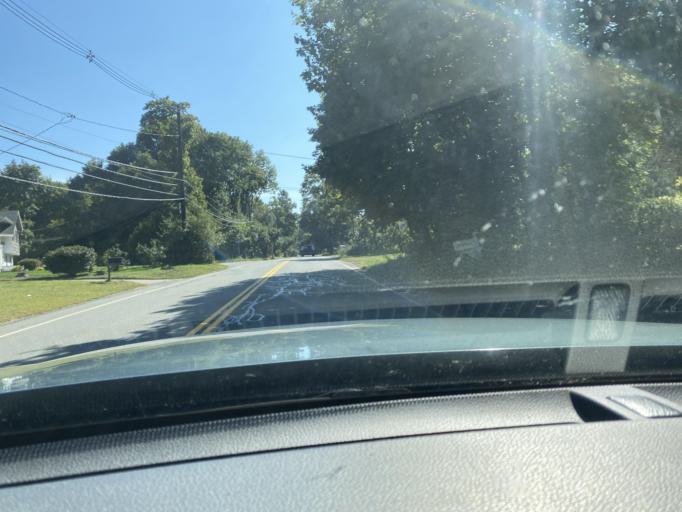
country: US
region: Massachusetts
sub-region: Norfolk County
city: Walpole
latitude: 42.1366
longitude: -71.2653
